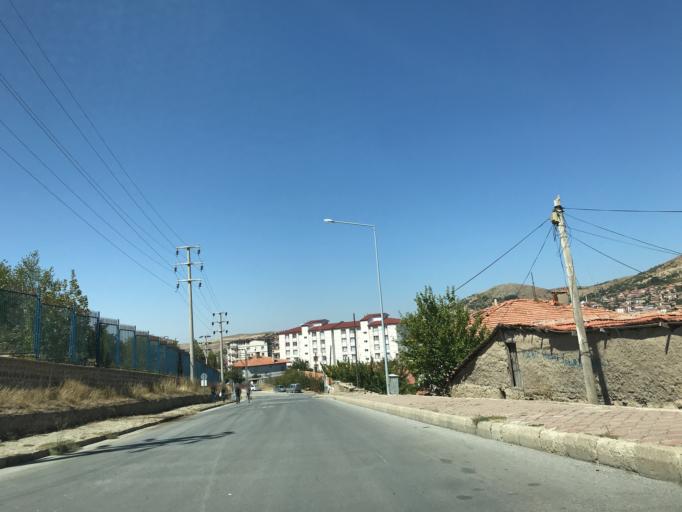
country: TR
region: Yozgat
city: Yozgat
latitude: 39.8183
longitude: 34.8185
